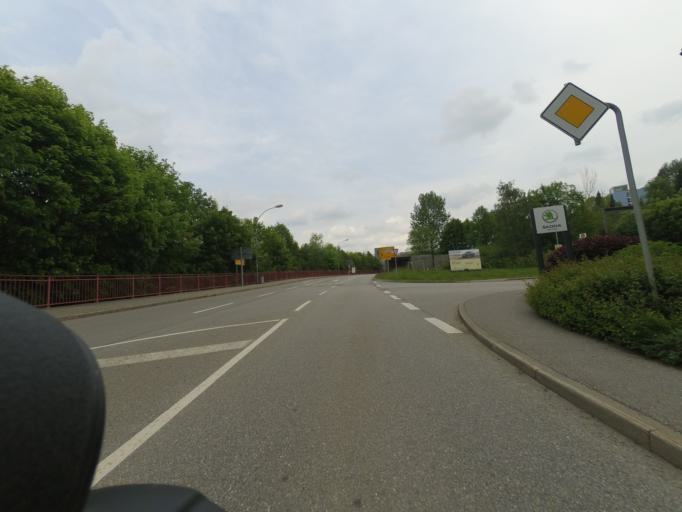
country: DE
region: Saxony
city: Zschopau
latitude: 50.7401
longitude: 13.0627
